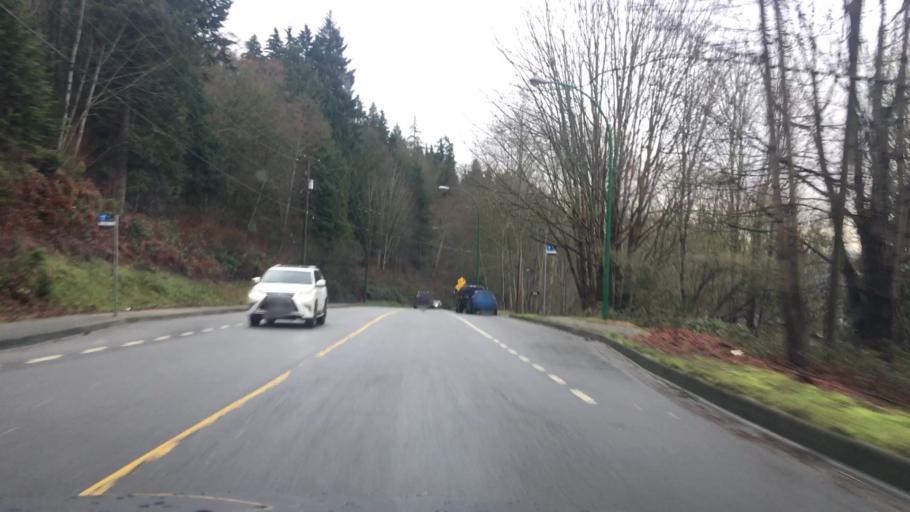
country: CA
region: British Columbia
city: Burnaby
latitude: 49.3078
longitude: -122.9799
